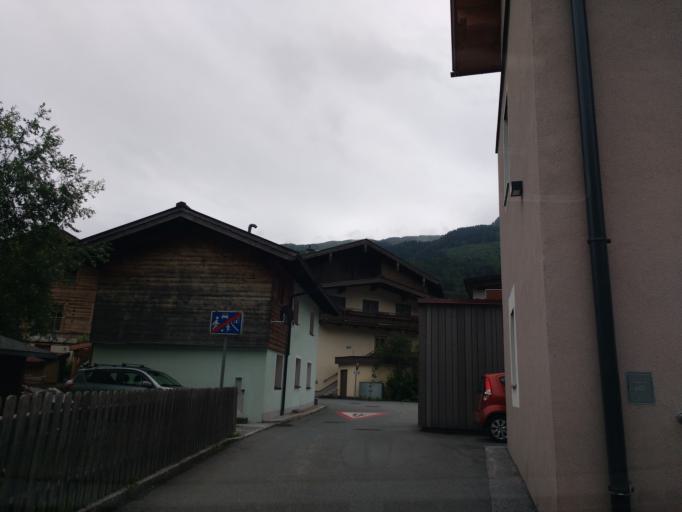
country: AT
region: Salzburg
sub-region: Politischer Bezirk Zell am See
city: Bramberg am Wildkogel
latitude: 47.2733
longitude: 12.3473
